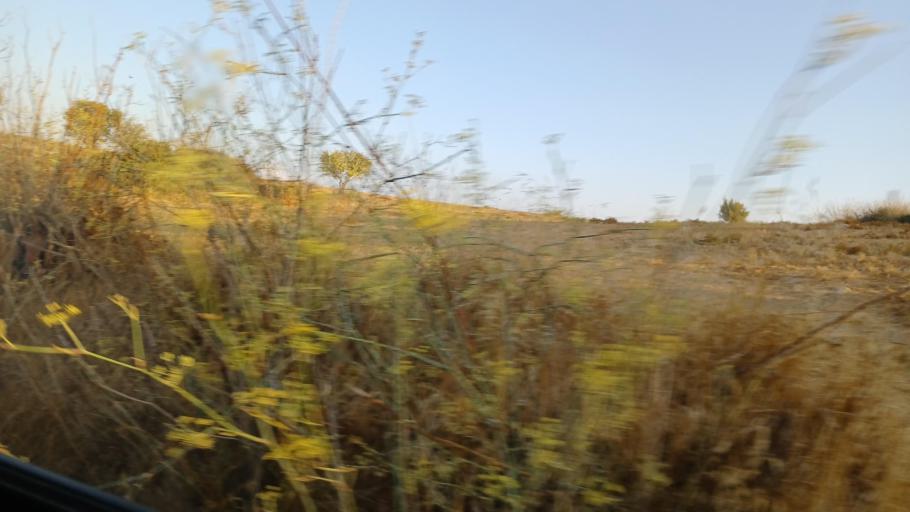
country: CY
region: Pafos
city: Tala
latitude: 34.9182
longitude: 32.4985
